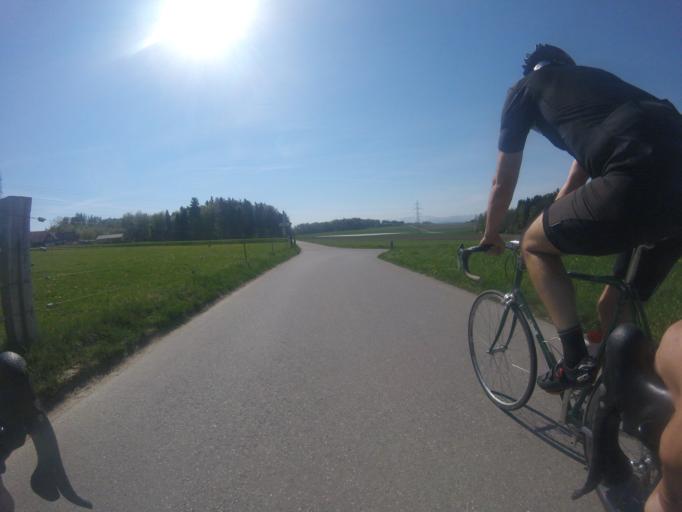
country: CH
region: Bern
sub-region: Bern-Mittelland District
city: Ferenbalm
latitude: 46.9400
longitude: 7.2251
